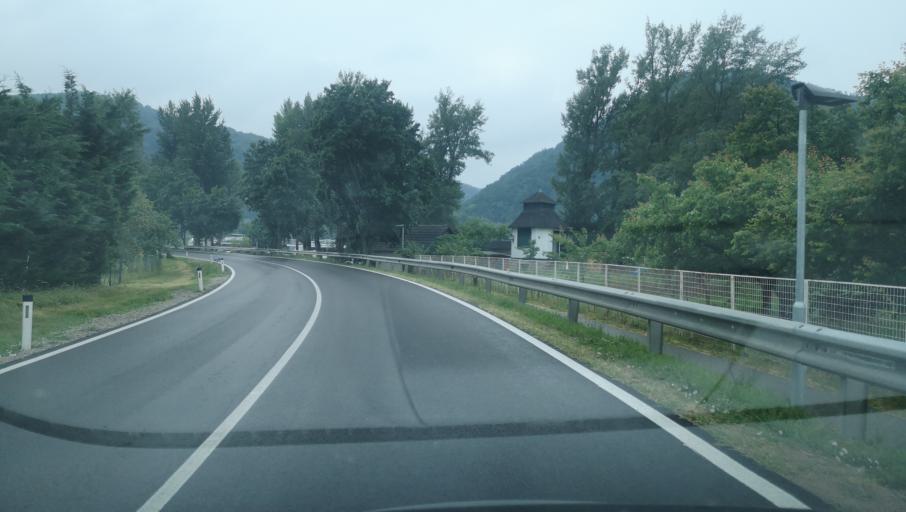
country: AT
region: Lower Austria
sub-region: Politischer Bezirk Krems
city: Durnstein
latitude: 48.3910
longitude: 15.5225
